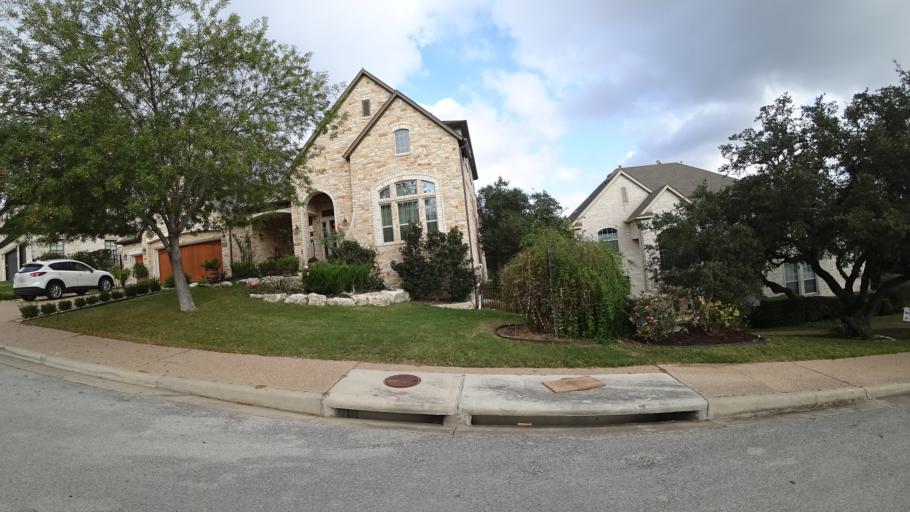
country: US
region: Texas
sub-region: Travis County
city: Barton Creek
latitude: 30.3138
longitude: -97.8960
